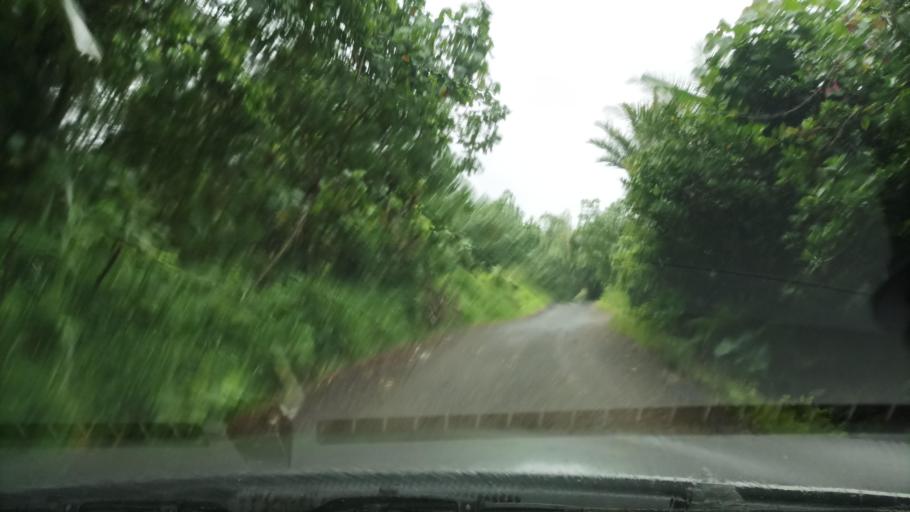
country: FM
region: Pohnpei
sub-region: Sokehs Municipality
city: Palikir - National Government Center
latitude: 6.8500
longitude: 158.1799
